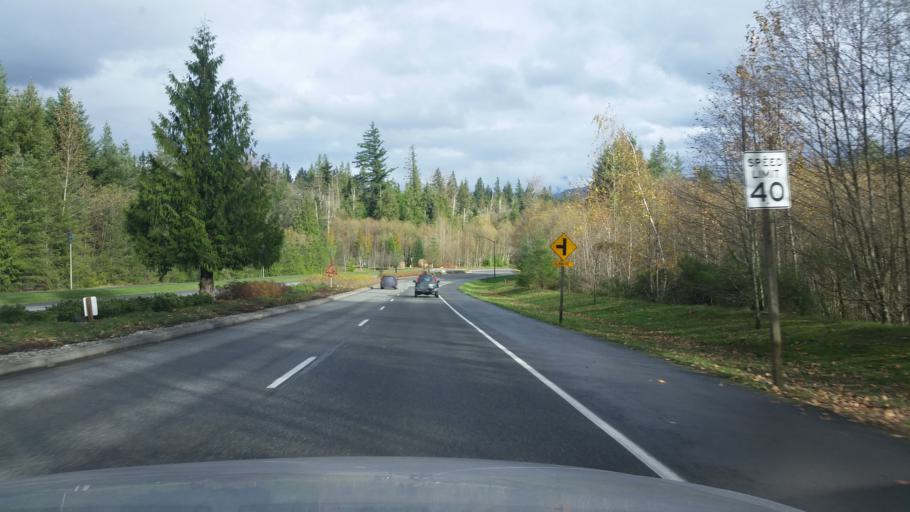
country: US
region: Washington
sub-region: King County
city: Snoqualmie
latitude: 47.5343
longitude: -121.8465
